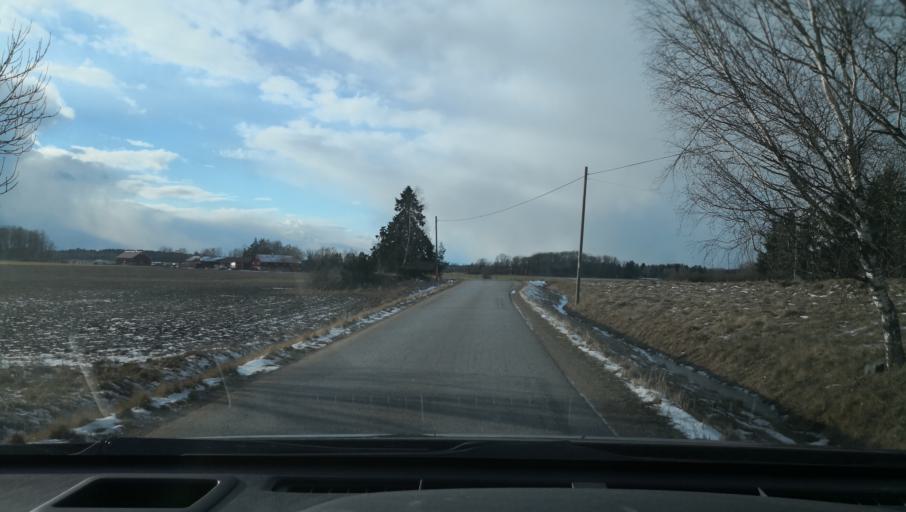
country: SE
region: Uppsala
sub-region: Enkopings Kommun
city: Irsta
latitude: 59.6962
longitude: 16.9565
